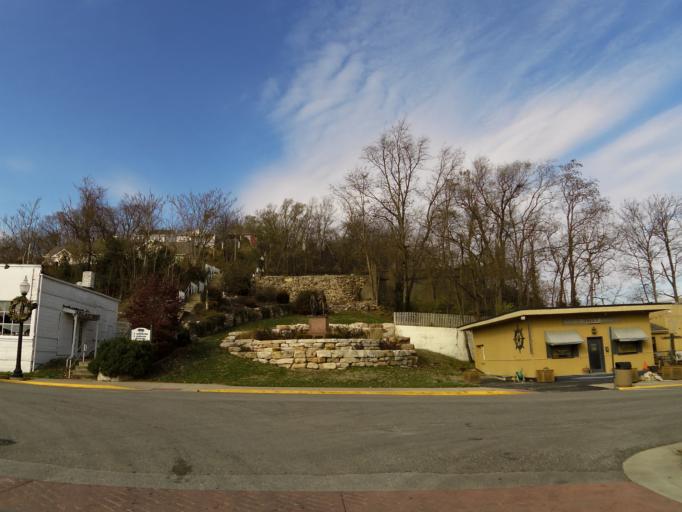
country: US
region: Missouri
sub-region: Marion County
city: Hannibal
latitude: 39.7128
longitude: -91.3579
